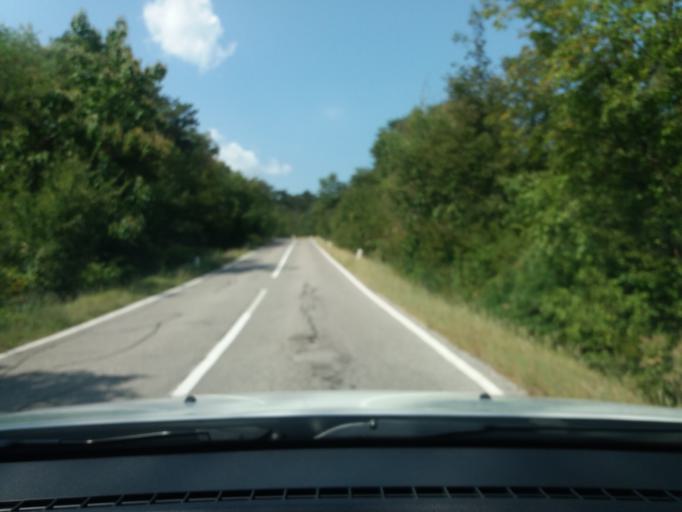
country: SI
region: Miren-Kostanjevica
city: Miren
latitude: 45.8790
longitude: 13.5960
